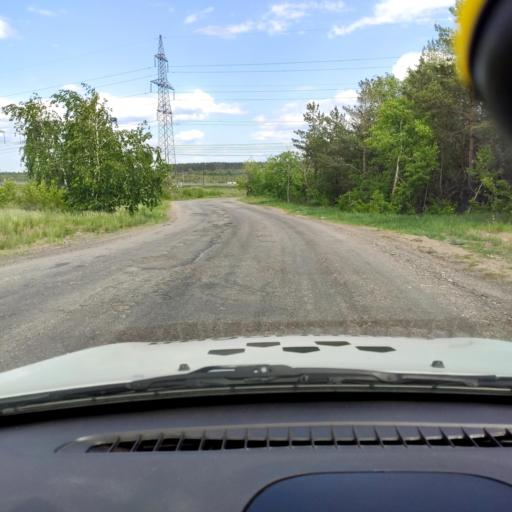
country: RU
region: Samara
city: Zhigulevsk
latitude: 53.5127
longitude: 49.5250
